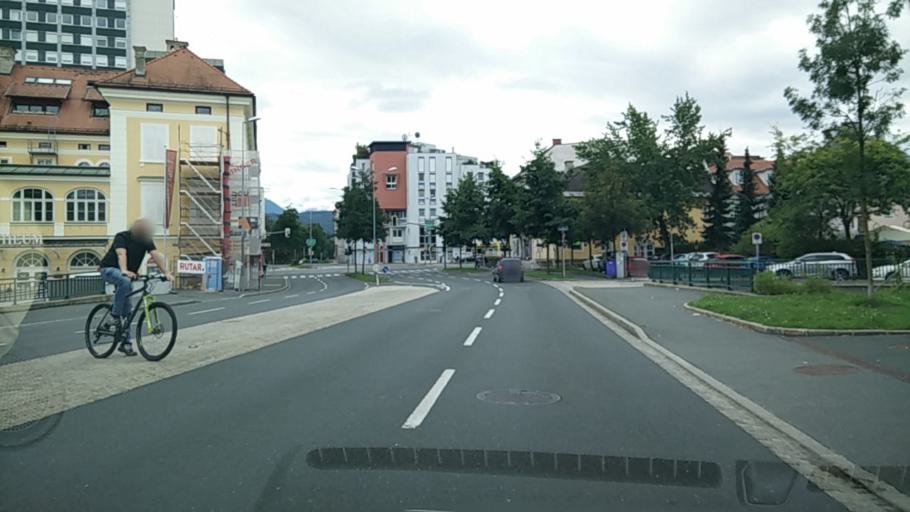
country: AT
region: Carinthia
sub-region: Klagenfurt am Woerthersee
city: Klagenfurt am Woerthersee
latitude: 46.6243
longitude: 14.3026
